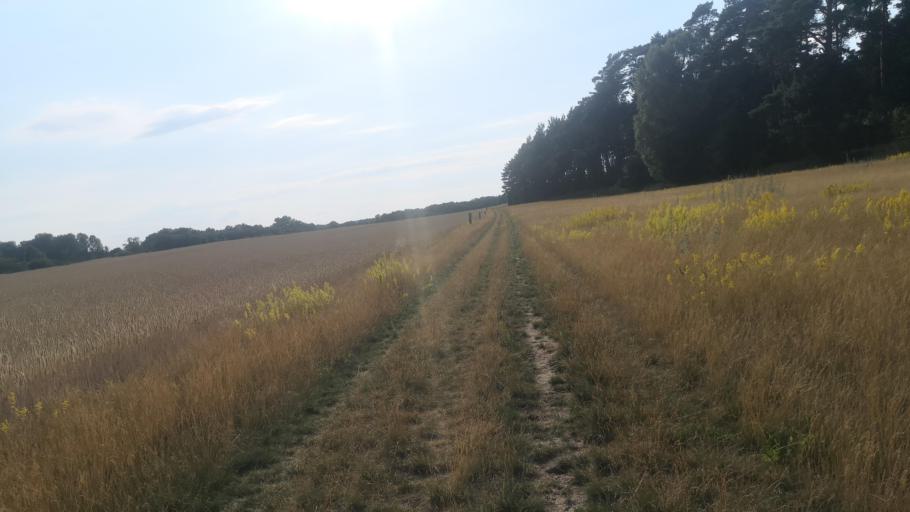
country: DE
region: Lower Saxony
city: Dahlenburg
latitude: 53.1973
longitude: 10.7396
